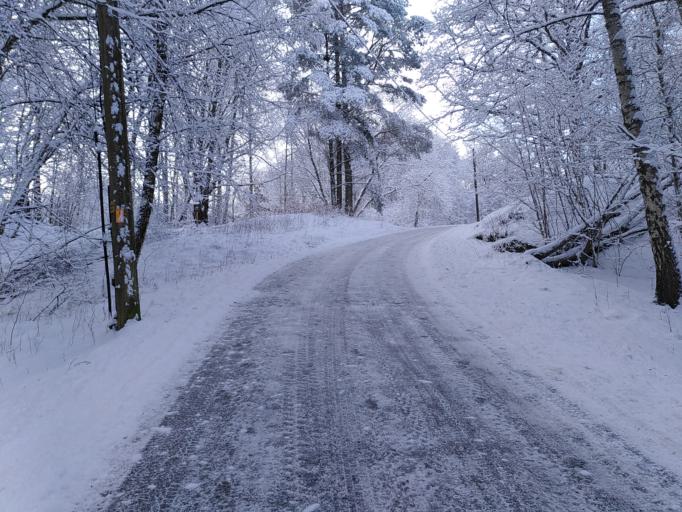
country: SE
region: Vaestra Goetaland
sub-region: Alingsas Kommun
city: Alingsas
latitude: 57.9246
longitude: 12.5647
